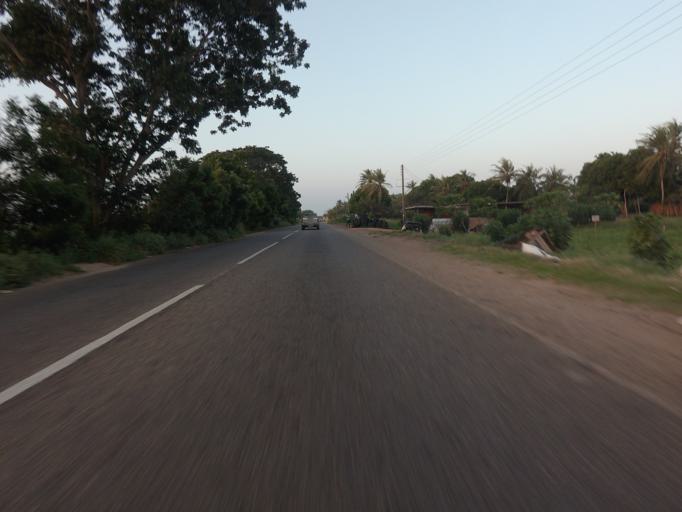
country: GH
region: Volta
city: Anloga
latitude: 5.8142
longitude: 0.9378
